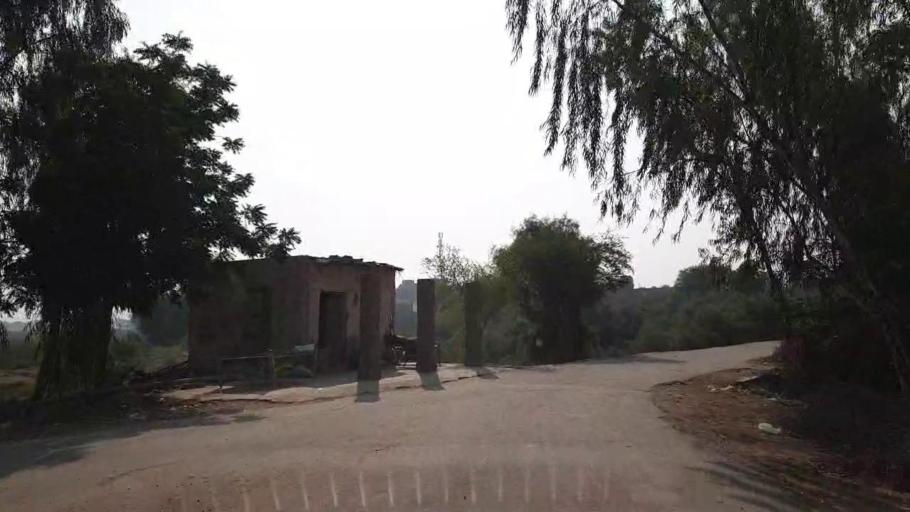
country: PK
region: Sindh
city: Sehwan
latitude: 26.4665
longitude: 67.7777
